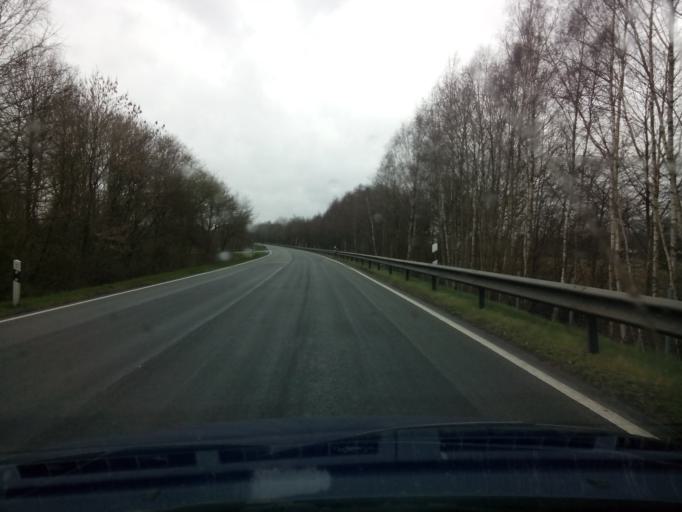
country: DE
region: Lower Saxony
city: Haselunne
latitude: 52.6885
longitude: 7.4810
